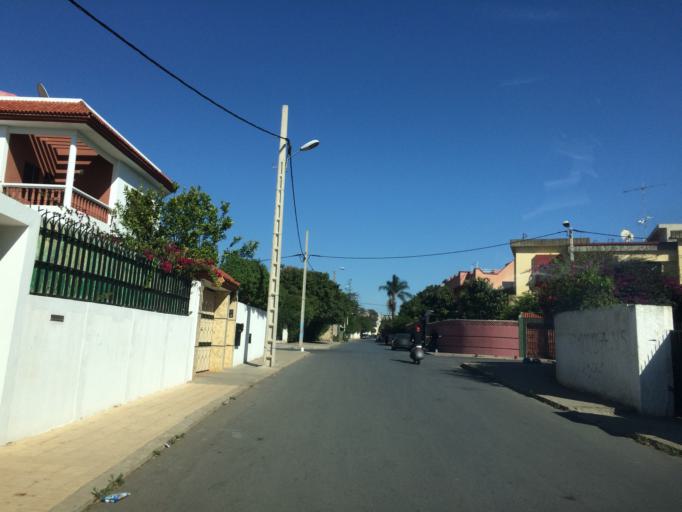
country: MA
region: Rabat-Sale-Zemmour-Zaer
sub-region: Rabat
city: Rabat
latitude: 33.9884
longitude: -6.8225
